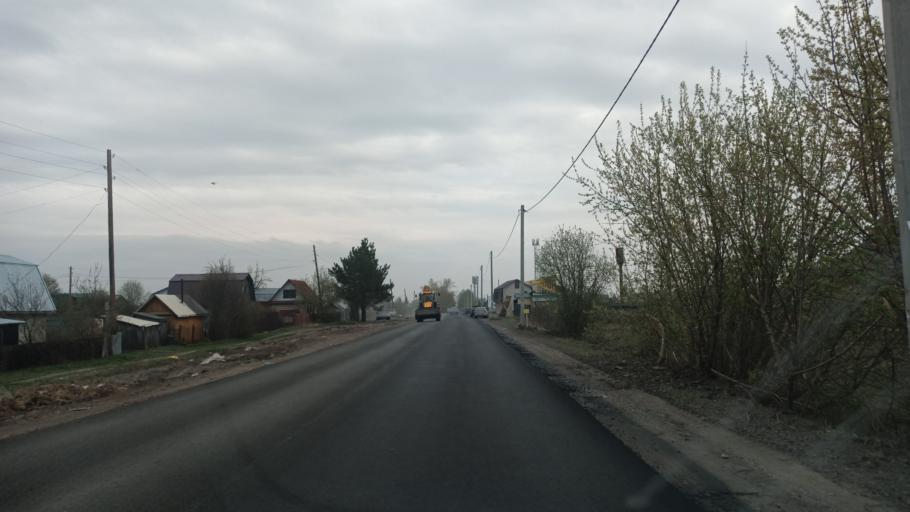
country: RU
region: Altai Krai
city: Yuzhnyy
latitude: 53.2299
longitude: 83.6890
